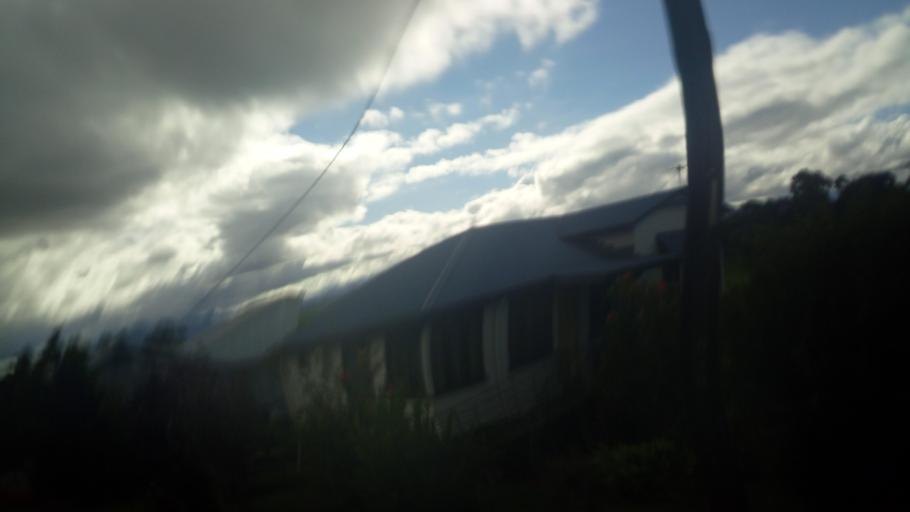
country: AU
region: Queensland
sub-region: Cassowary Coast
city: Innisfail
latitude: -17.5526
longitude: 145.9616
